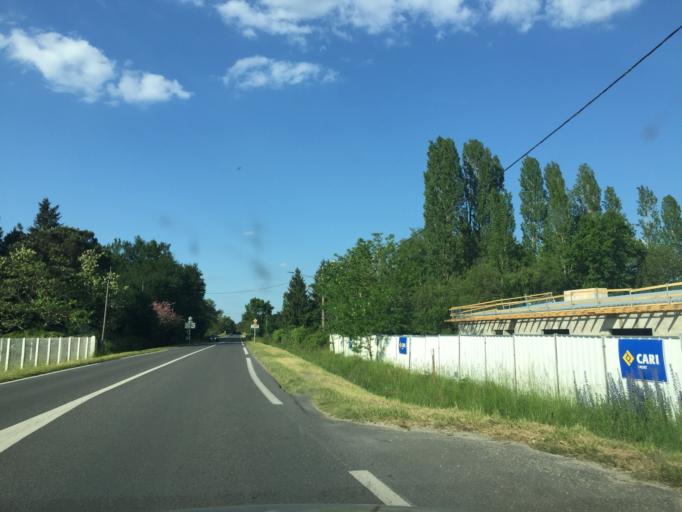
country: FR
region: Aquitaine
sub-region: Departement de la Gironde
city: Saint-Denis-de-Pile
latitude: 44.9940
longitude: -0.1962
